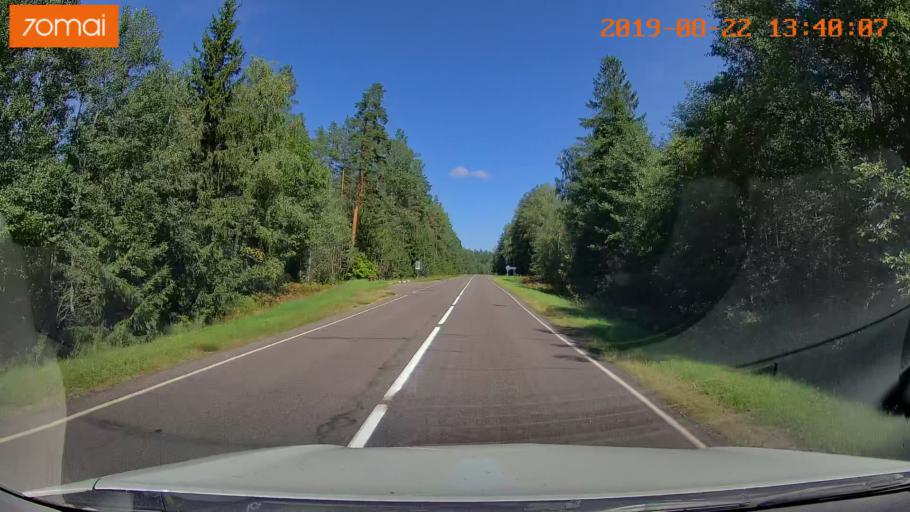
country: BY
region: Minsk
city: Staryya Darohi
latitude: 53.2334
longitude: 28.3613
